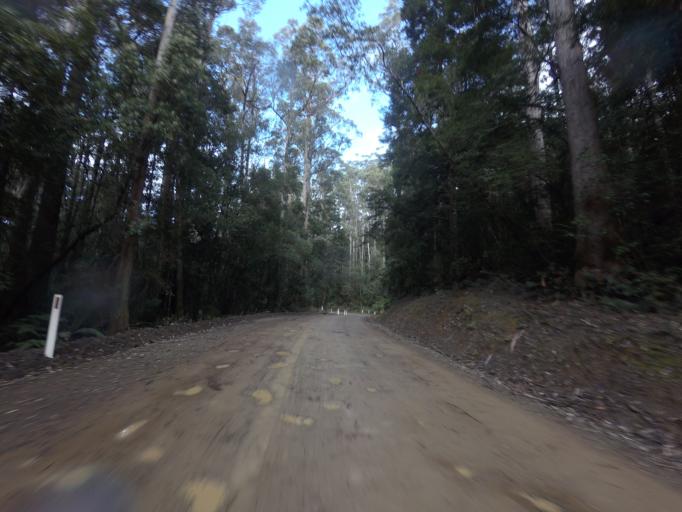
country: AU
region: Tasmania
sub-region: Huon Valley
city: Geeveston
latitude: -43.5741
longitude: 146.8882
